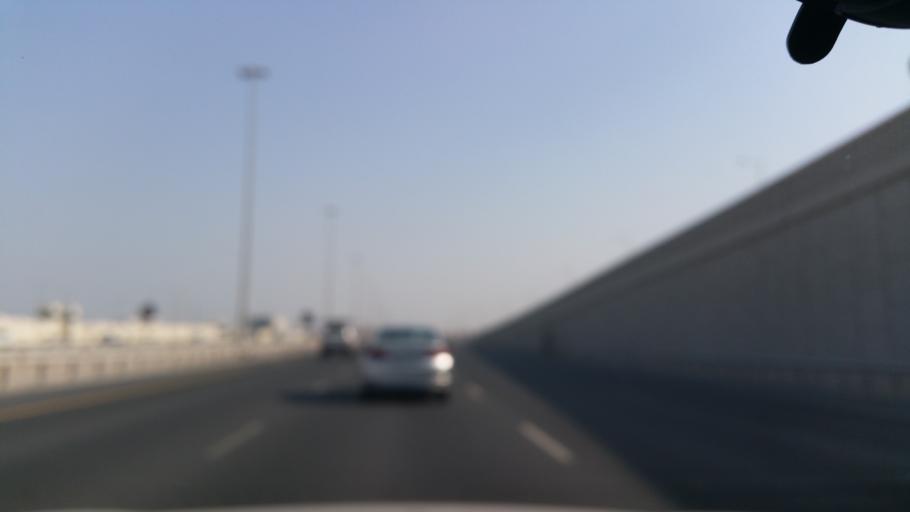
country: QA
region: Baladiyat Umm Salal
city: Umm Salal Muhammad
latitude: 25.3628
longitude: 51.4486
